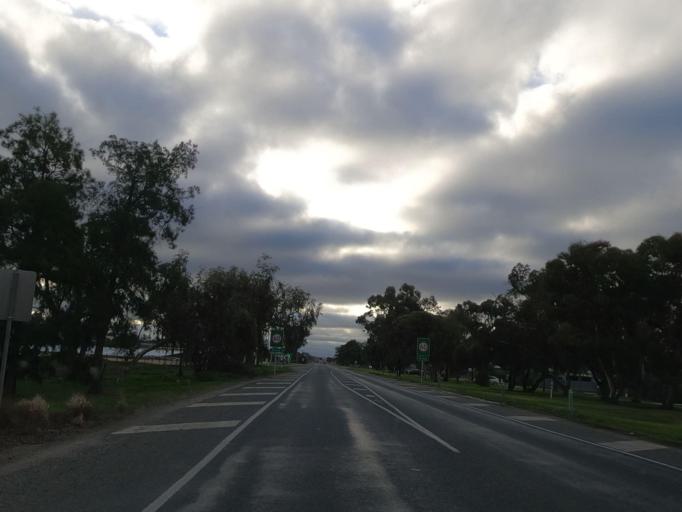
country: AU
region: Victoria
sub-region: Swan Hill
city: Swan Hill
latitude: -35.7422
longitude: 143.9205
